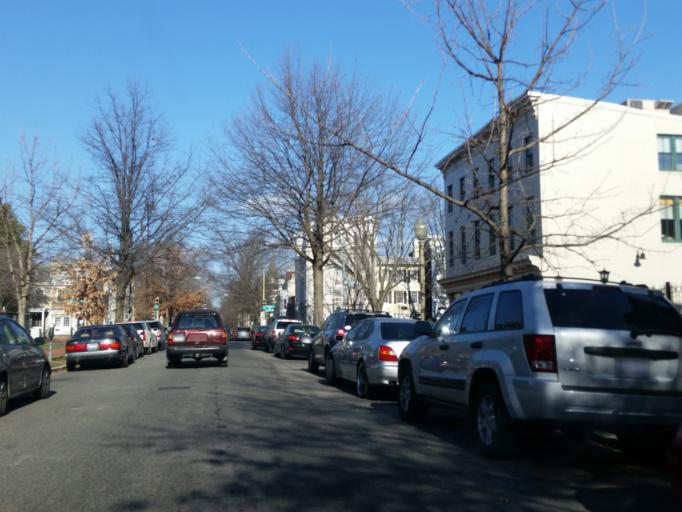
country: US
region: Washington, D.C.
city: Washington, D.C.
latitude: 38.8893
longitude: -77.0021
